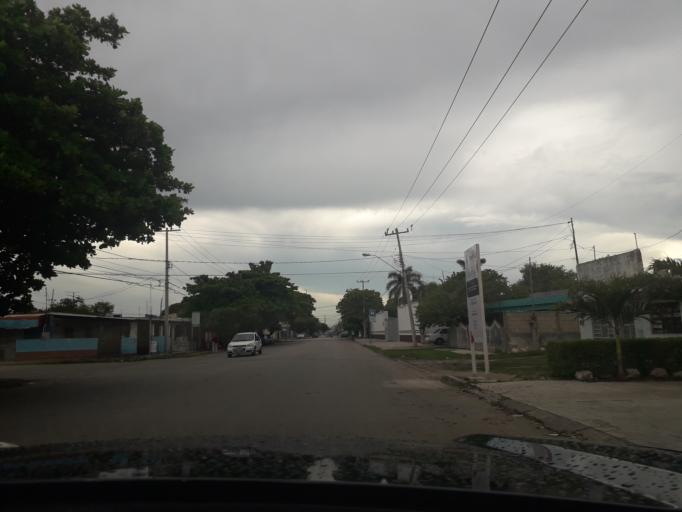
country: MX
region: Yucatan
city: Merida
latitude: 20.9590
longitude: -89.6470
